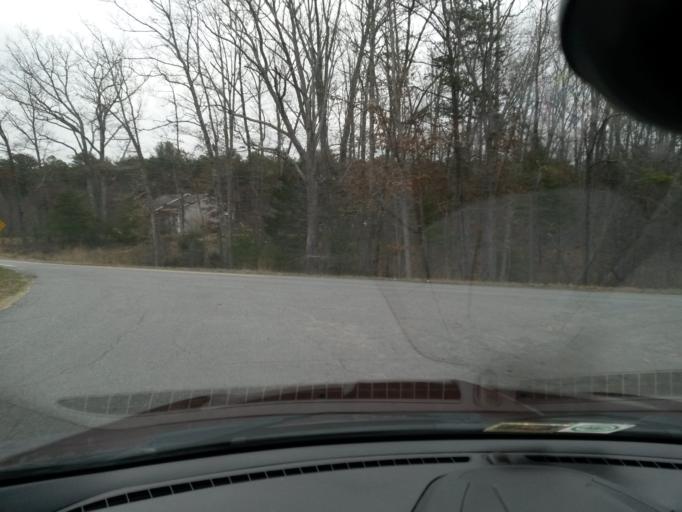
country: US
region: Virginia
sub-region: Bath County
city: Warm Springs
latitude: 37.9905
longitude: -79.6001
